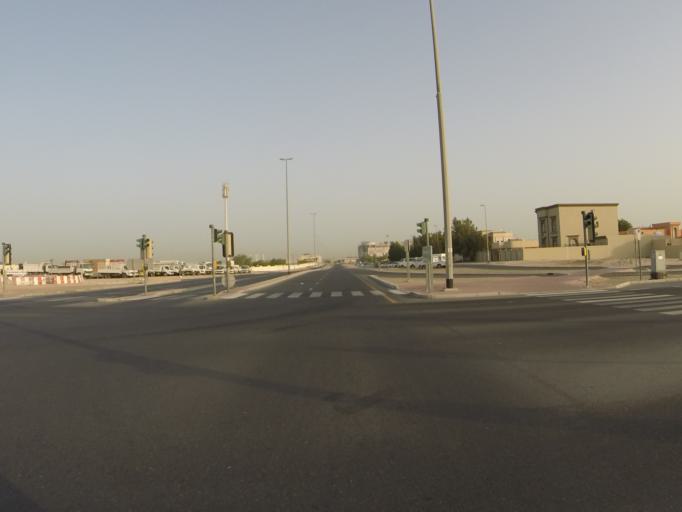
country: AE
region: Dubai
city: Dubai
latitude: 25.1643
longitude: 55.2467
